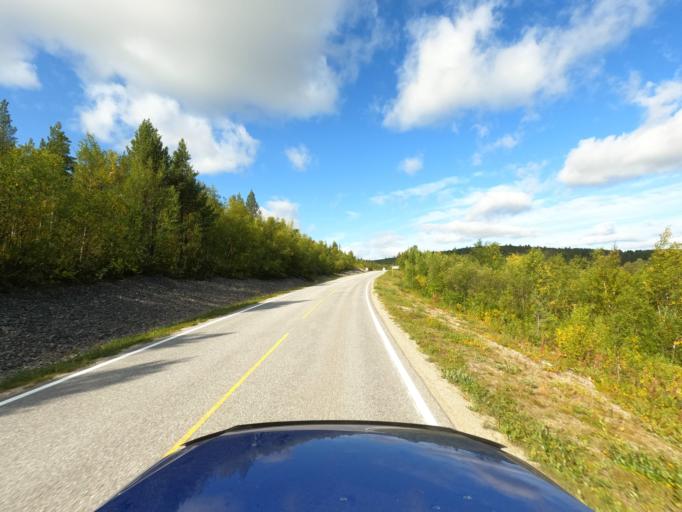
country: NO
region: Finnmark Fylke
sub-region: Karasjok
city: Karasjohka
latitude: 69.4833
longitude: 25.5116
